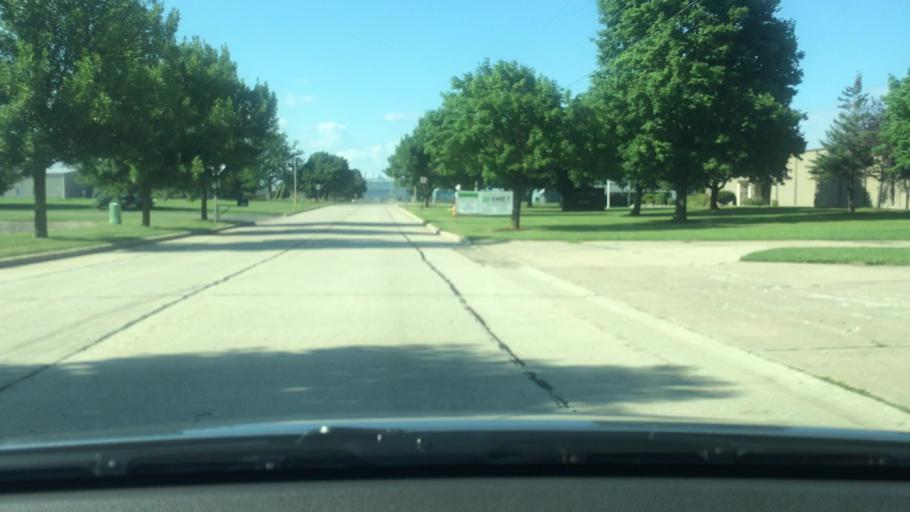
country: US
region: Wisconsin
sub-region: Winnebago County
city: Oshkosh
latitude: 43.9767
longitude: -88.5507
